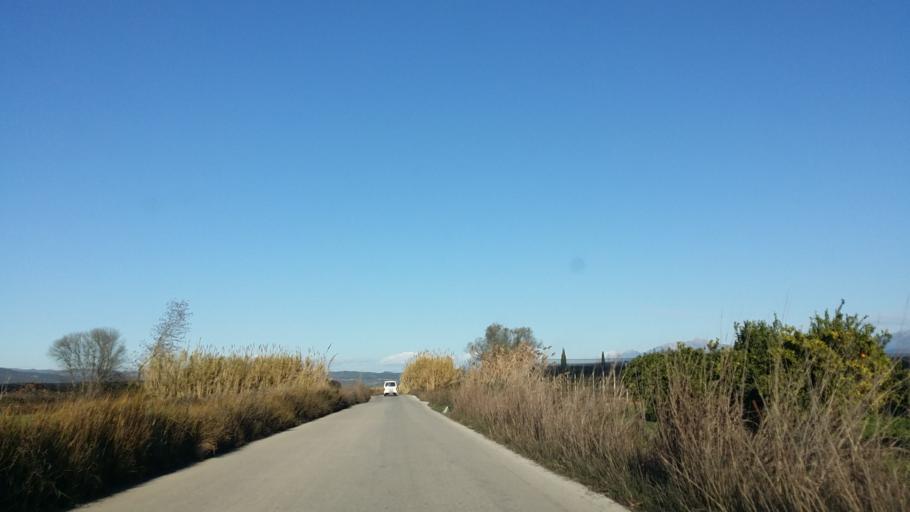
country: GR
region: West Greece
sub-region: Nomos Aitolias kai Akarnanias
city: Lepenou
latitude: 38.6422
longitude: 21.2505
